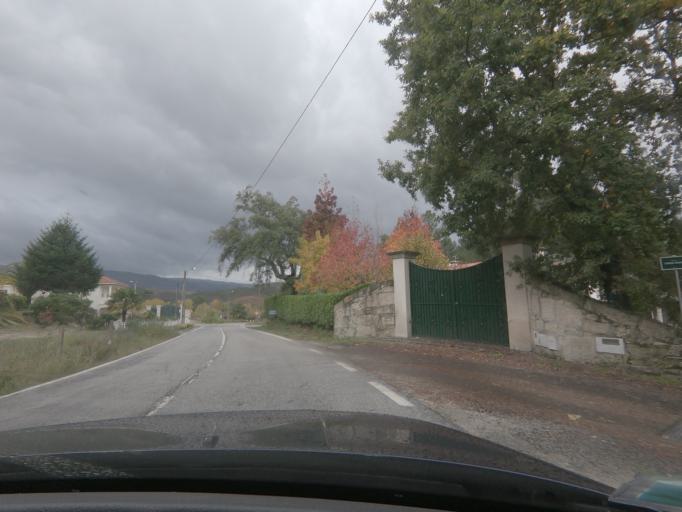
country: PT
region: Vila Real
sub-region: Mondim de Basto
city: Mondim de Basto
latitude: 41.3963
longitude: -7.9598
